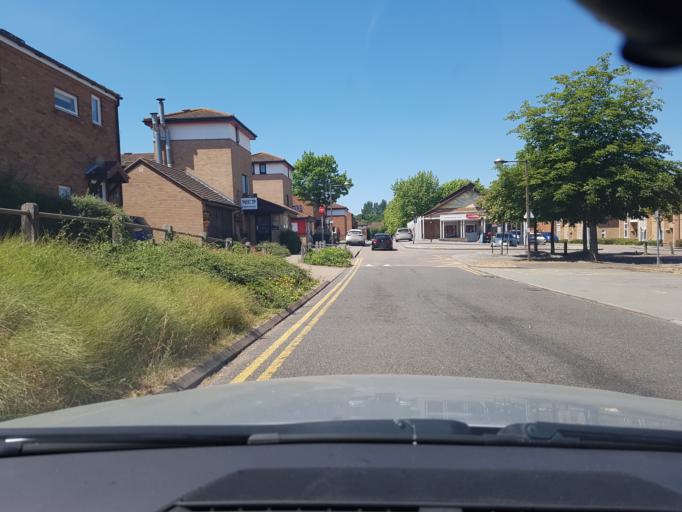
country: GB
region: England
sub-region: Milton Keynes
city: Loughton
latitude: 52.0380
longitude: -0.8011
